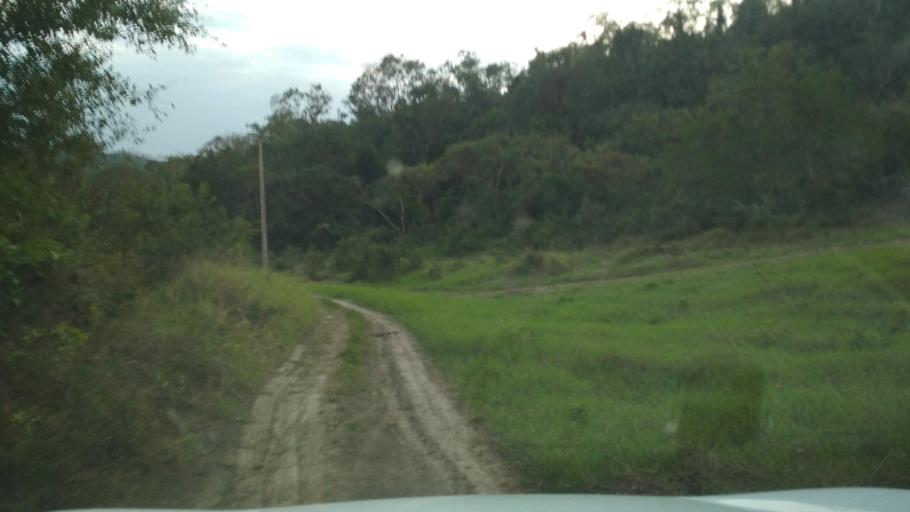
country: MX
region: Veracruz
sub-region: Poza Rica de Hidalgo
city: Arroyo del Maiz Uno
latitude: 20.4872
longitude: -97.3902
